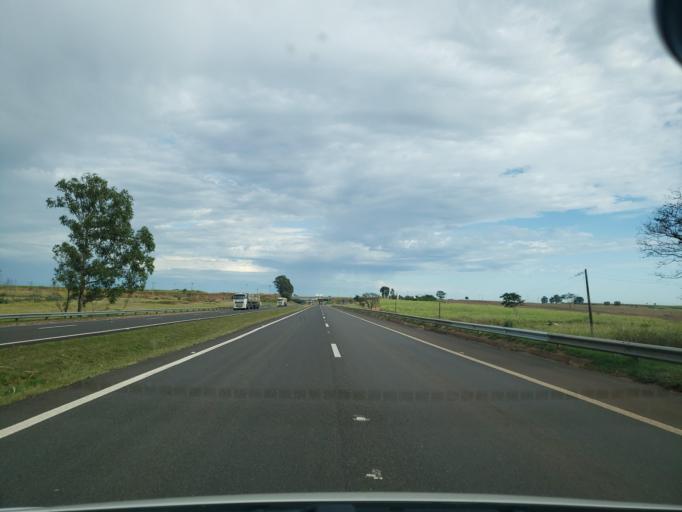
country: BR
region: Sao Paulo
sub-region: Dois Corregos
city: Dois Corregos
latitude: -22.2656
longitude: -48.4375
